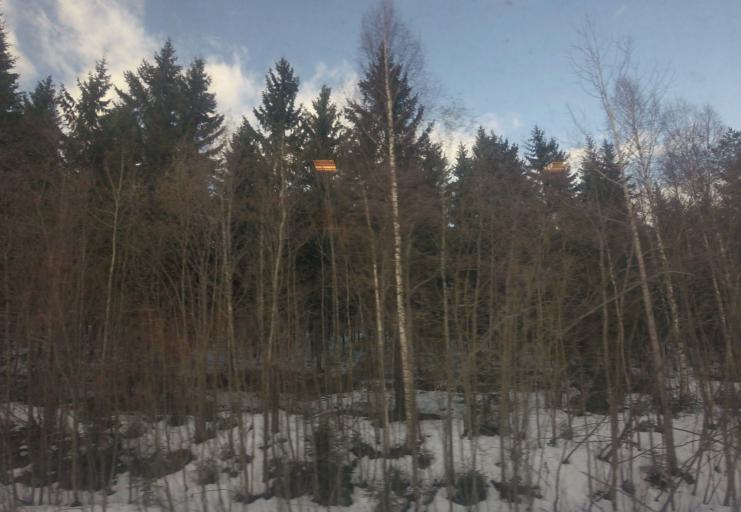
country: FI
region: Southern Savonia
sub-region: Savonlinna
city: Kerimaeki
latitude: 61.8557
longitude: 29.1392
